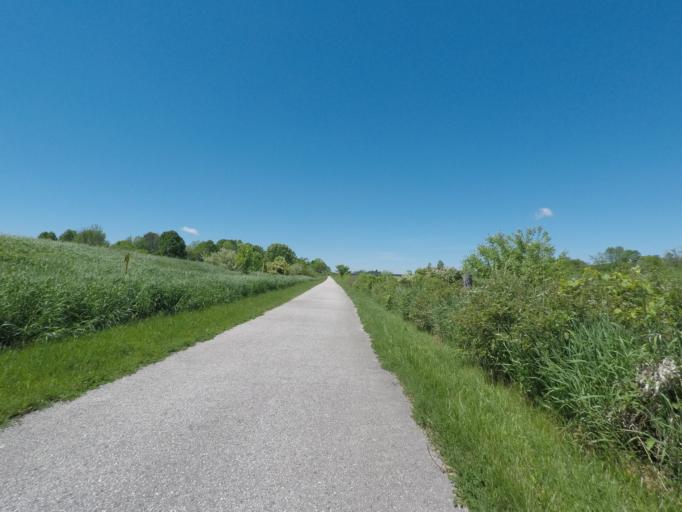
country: US
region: Wisconsin
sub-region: Sheboygan County
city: Kohler
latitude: 43.7512
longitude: -87.7954
